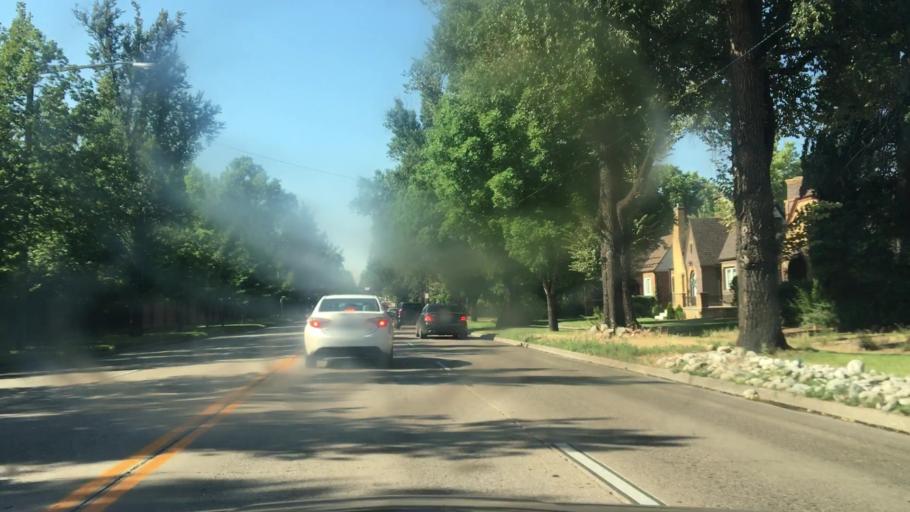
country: US
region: Colorado
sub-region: Arapahoe County
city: Glendale
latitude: 39.7066
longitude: -104.9593
